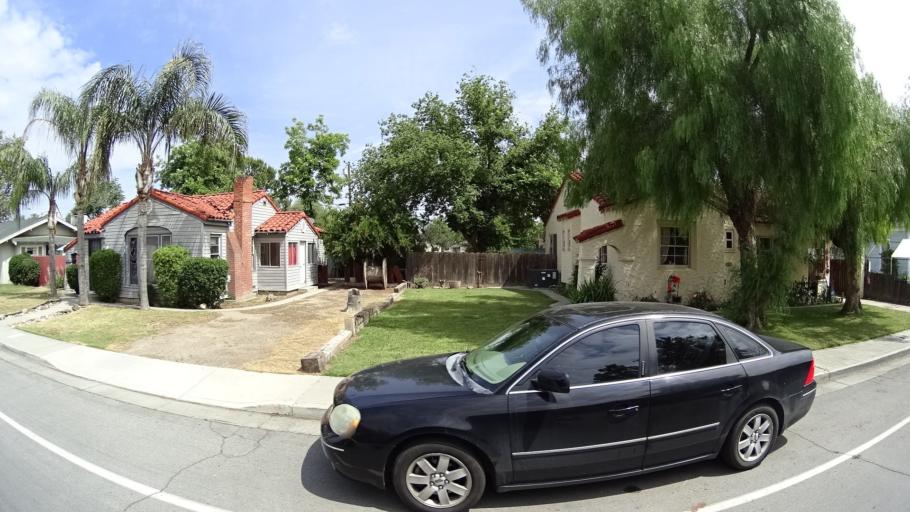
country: US
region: California
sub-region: Kings County
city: Hanford
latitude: 36.3349
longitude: -119.6500
